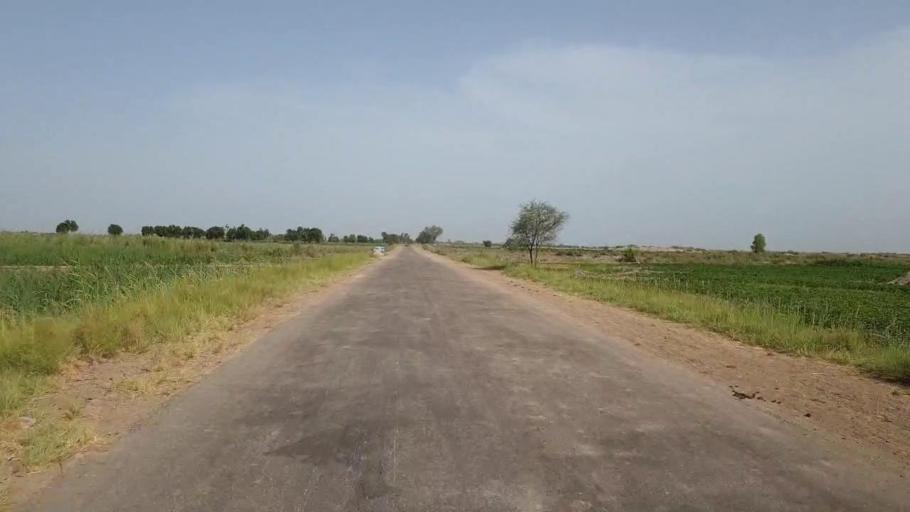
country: PK
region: Sindh
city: Sakrand
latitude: 26.2816
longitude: 68.2666
